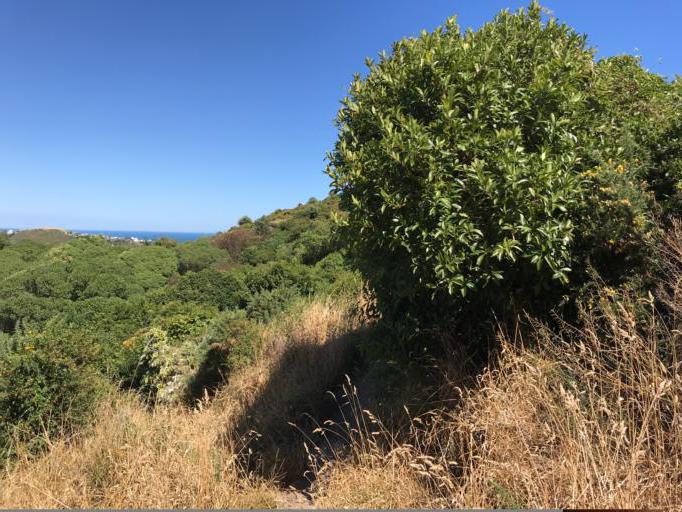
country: NZ
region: Wellington
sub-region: Wellington City
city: Brooklyn
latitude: -41.3314
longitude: 174.7664
